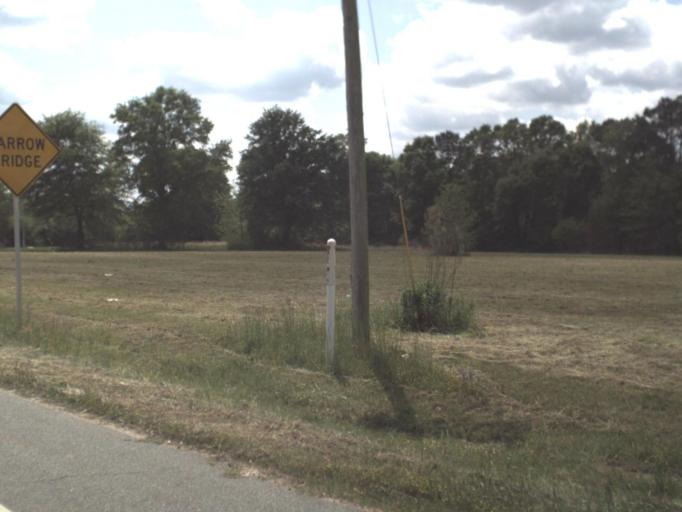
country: US
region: Alabama
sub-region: Escambia County
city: Atmore
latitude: 30.9545
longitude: -87.4865
